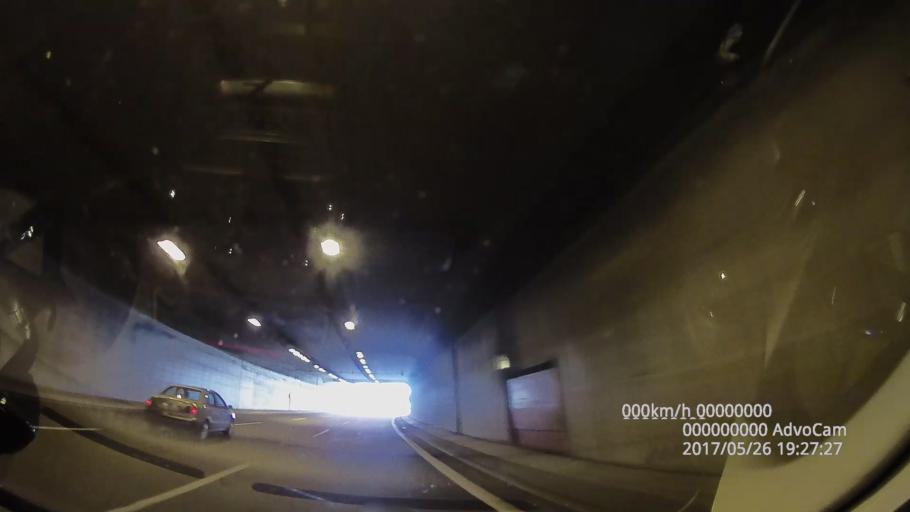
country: GR
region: Central Macedonia
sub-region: Nomos Thessalonikis
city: Nea Malgara
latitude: 40.5968
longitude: 22.6707
